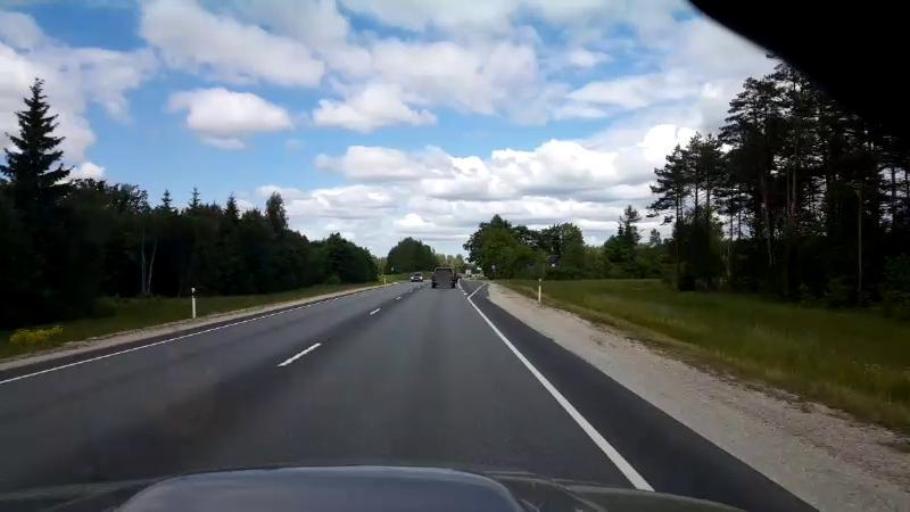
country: EE
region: Harju
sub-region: Nissi vald
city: Riisipere
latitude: 59.0782
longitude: 24.4552
